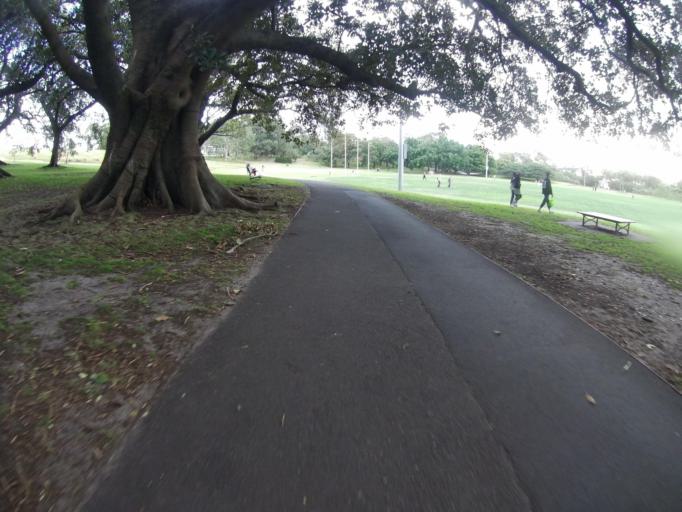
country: AU
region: New South Wales
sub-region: City of Sydney
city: Redfern
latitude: -33.8946
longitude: 151.2185
